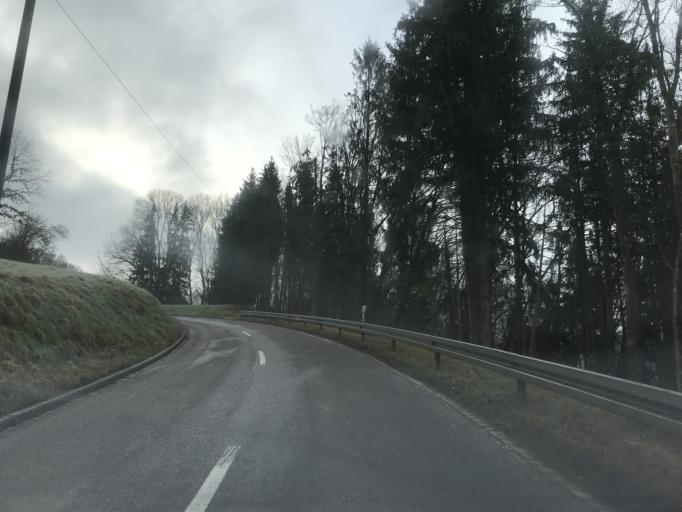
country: DE
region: Baden-Wuerttemberg
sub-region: Freiburg Region
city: Wehr
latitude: 47.6238
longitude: 7.9090
